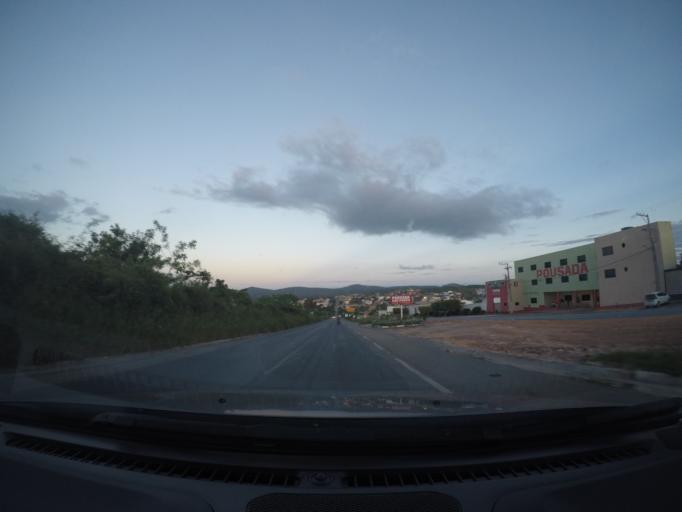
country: BR
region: Bahia
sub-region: Seabra
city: Seabra
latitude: -12.4296
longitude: -41.7835
